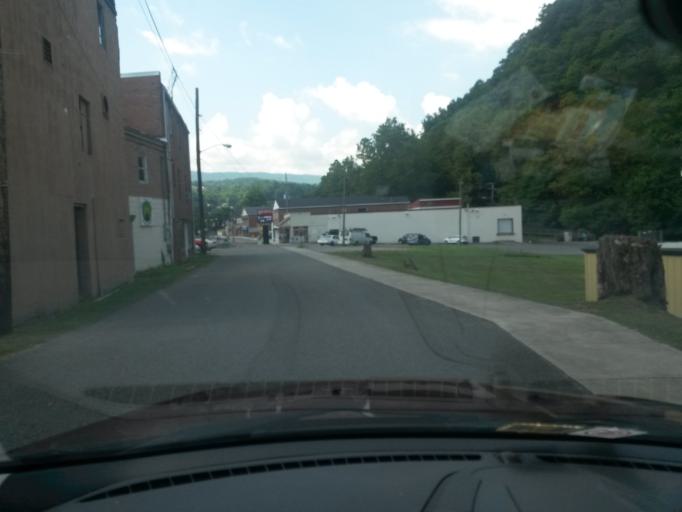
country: US
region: Virginia
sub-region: Giles County
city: Narrows
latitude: 37.3326
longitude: -80.8112
